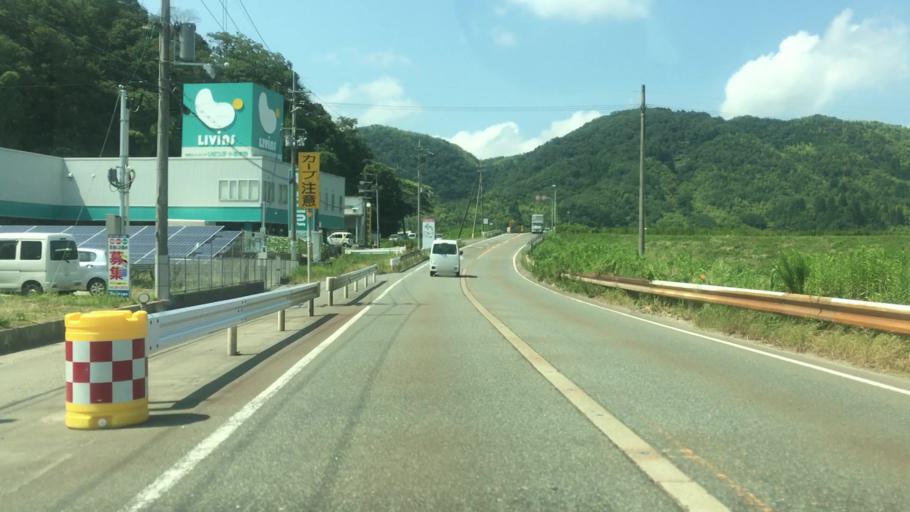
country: JP
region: Hyogo
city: Toyooka
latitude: 35.5617
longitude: 134.7958
